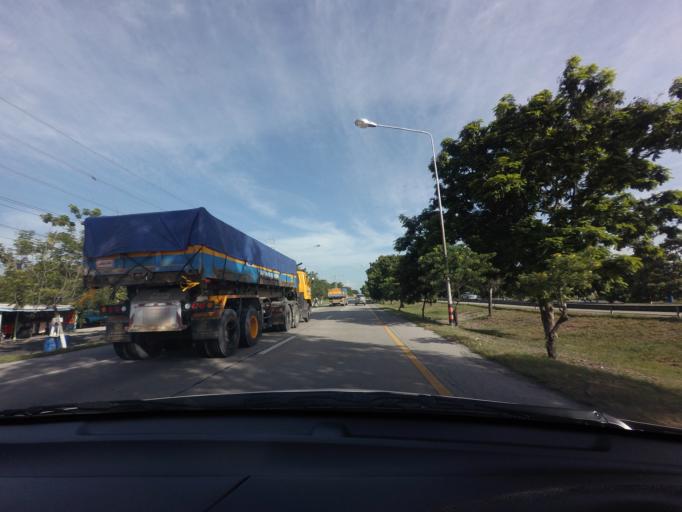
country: TH
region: Suphan Buri
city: Bang Pla Ma
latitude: 14.3833
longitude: 100.1767
